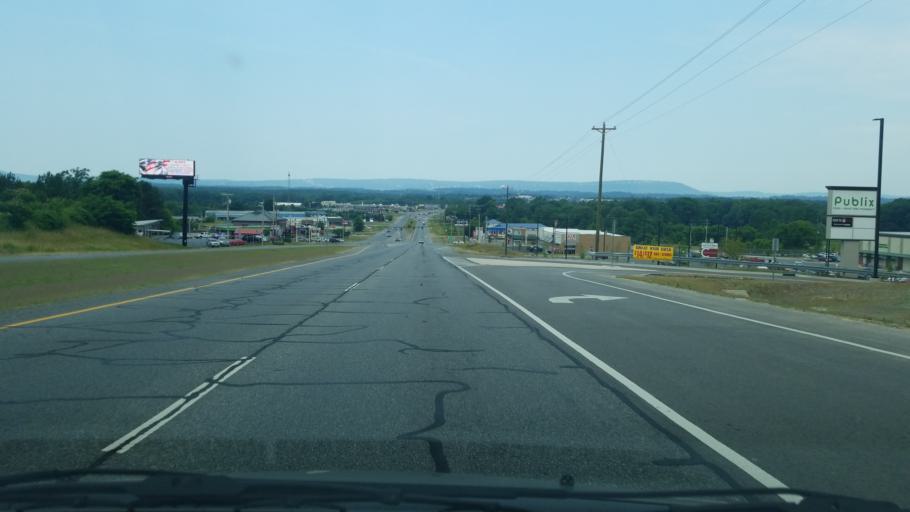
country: US
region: Georgia
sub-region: Catoosa County
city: Indian Springs
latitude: 34.9366
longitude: -85.2028
